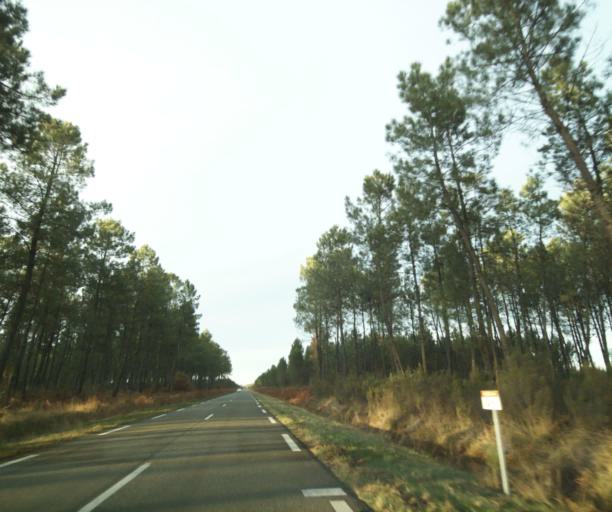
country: FR
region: Aquitaine
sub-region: Departement des Landes
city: Roquefort
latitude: 44.1773
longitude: -0.1439
